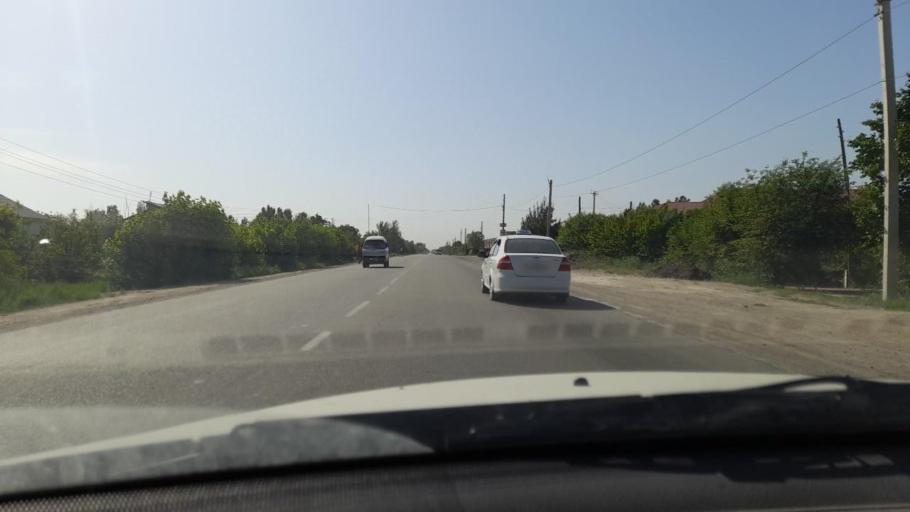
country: UZ
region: Bukhara
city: Romiton
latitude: 39.9064
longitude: 64.4003
